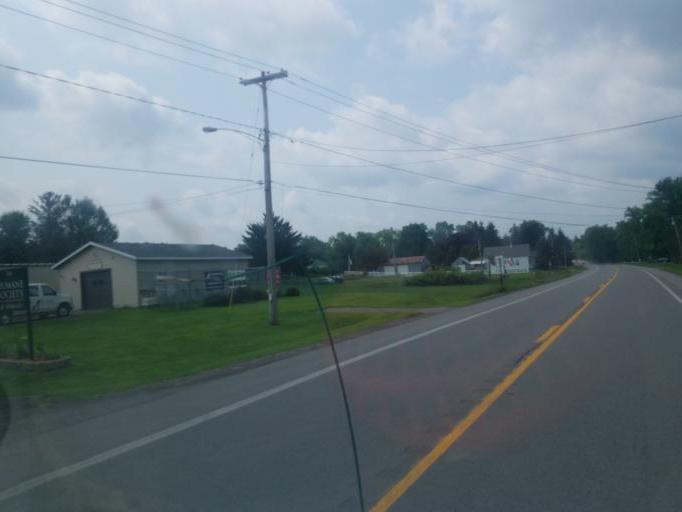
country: US
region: New York
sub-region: Herkimer County
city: Herkimer
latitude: 43.0181
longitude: -74.9586
